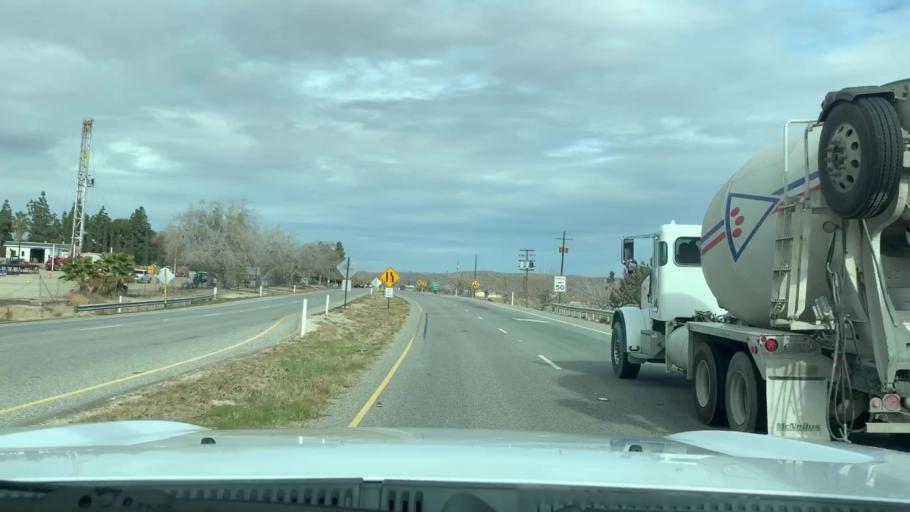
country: US
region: California
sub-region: Kern County
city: South Taft
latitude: 35.1377
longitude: -119.4471
